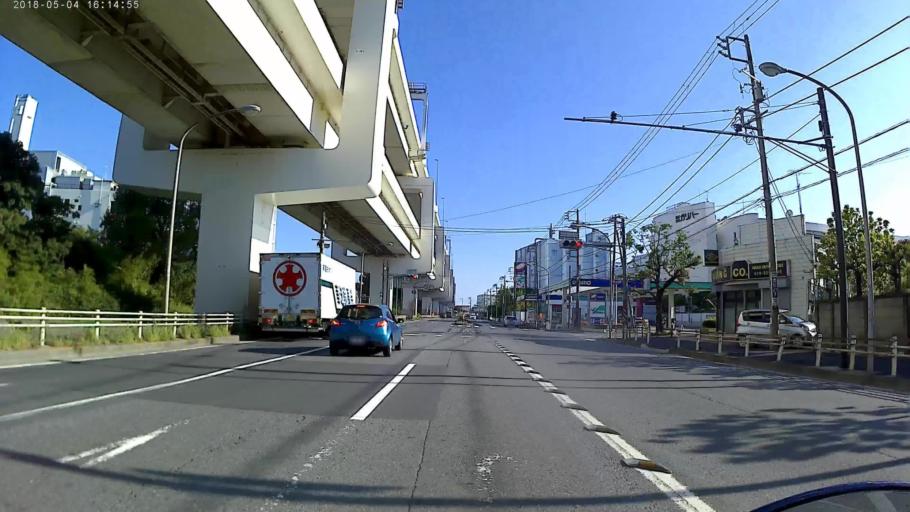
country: JP
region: Kanagawa
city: Yokohama
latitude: 35.4810
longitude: 139.6751
